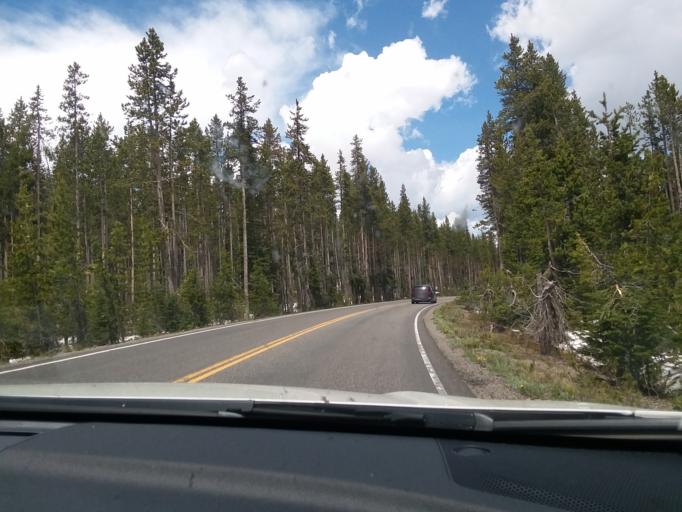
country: US
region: Montana
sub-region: Gallatin County
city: West Yellowstone
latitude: 44.2001
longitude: -110.6597
